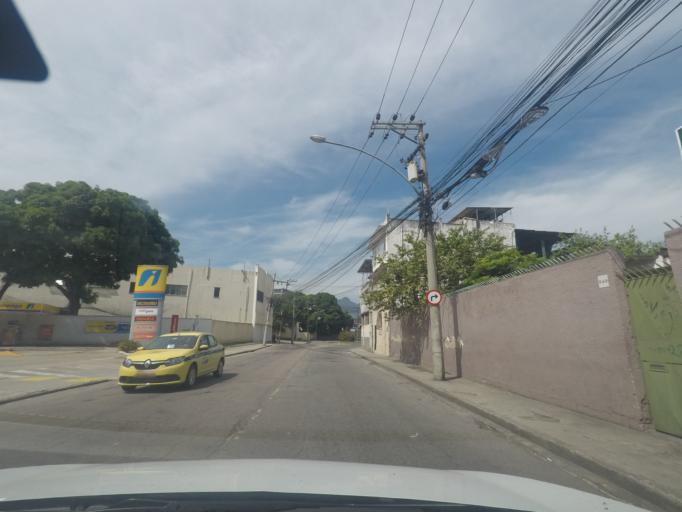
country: BR
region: Rio de Janeiro
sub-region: Rio De Janeiro
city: Rio de Janeiro
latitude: -22.9083
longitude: -43.2201
